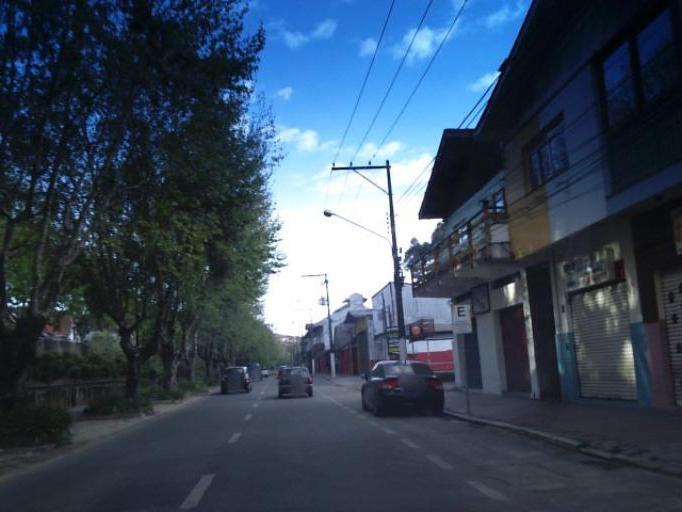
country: BR
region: Sao Paulo
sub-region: Campos Do Jordao
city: Campos do Jordao
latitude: -22.7309
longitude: -45.5834
